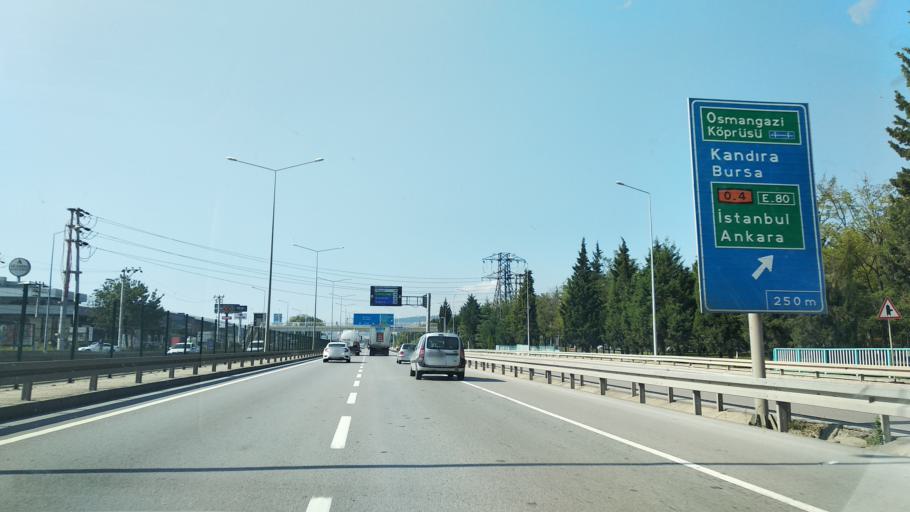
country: TR
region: Kocaeli
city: Kullar
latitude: 40.7601
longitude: 29.9776
